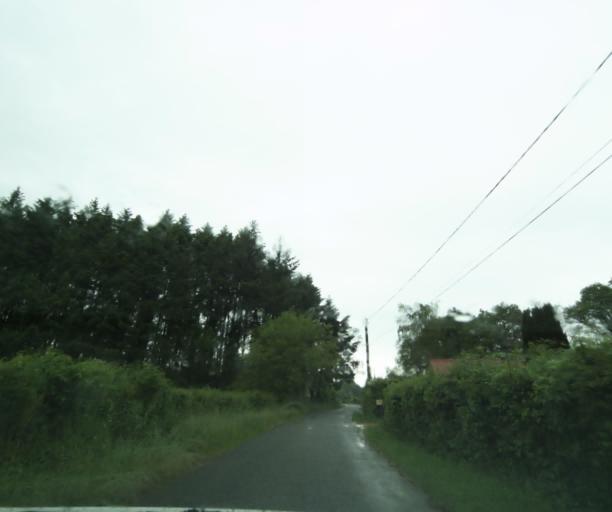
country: FR
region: Bourgogne
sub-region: Departement de Saone-et-Loire
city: Ciry-le-Noble
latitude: 46.5371
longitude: 4.3015
